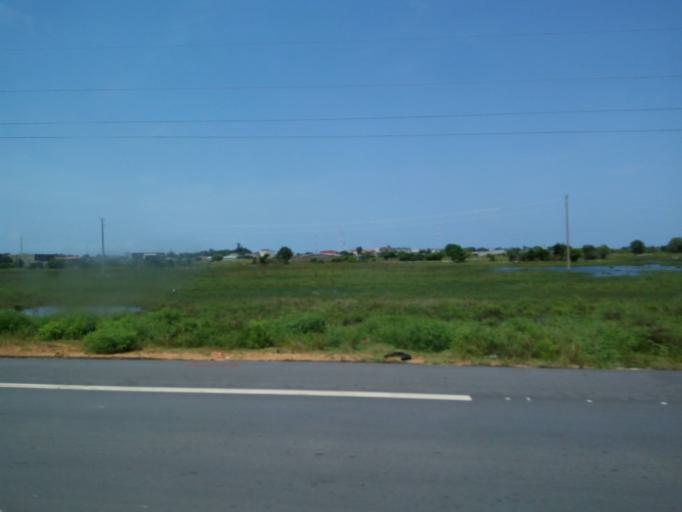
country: CI
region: Sud-Comoe
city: Grand-Bassam
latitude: 5.2271
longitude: -3.7417
